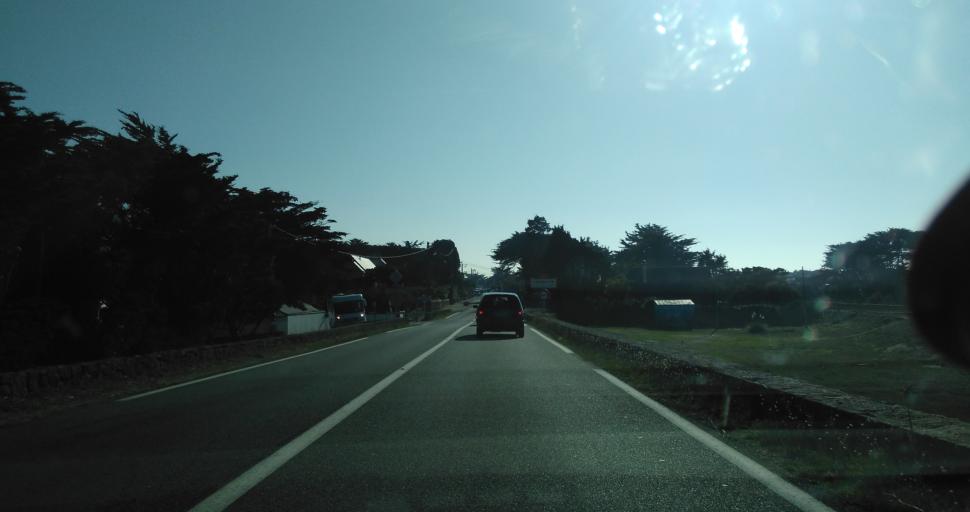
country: FR
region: Brittany
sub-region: Departement du Morbihan
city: Saint-Pierre-Quiberon
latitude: 47.5406
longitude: -3.1351
